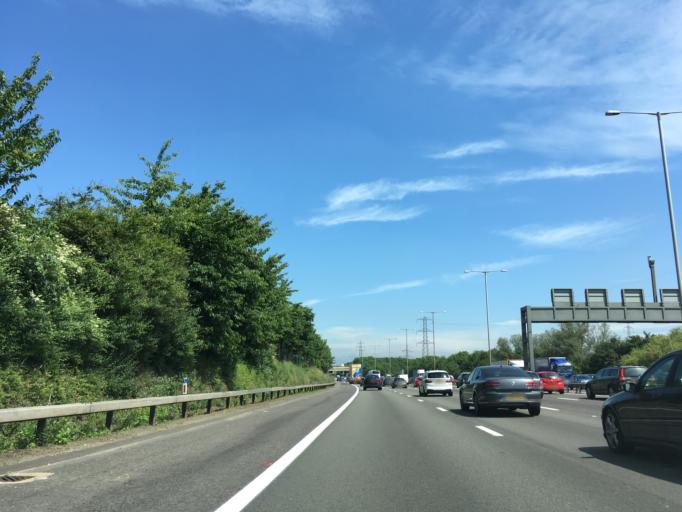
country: GB
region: England
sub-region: Buckinghamshire
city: Iver
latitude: 51.5178
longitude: -0.4996
